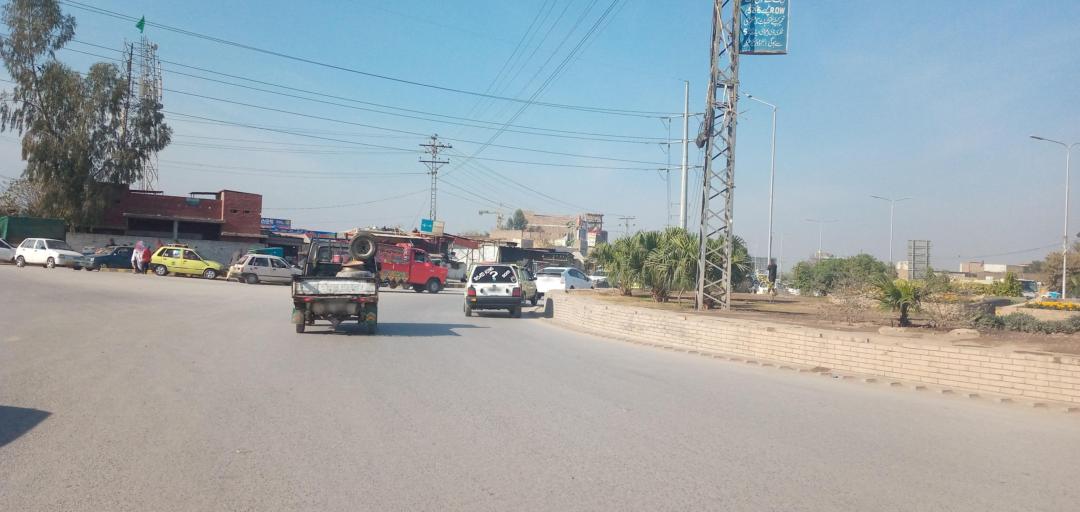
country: PK
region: Khyber Pakhtunkhwa
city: Peshawar
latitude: 33.9606
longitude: 71.5051
